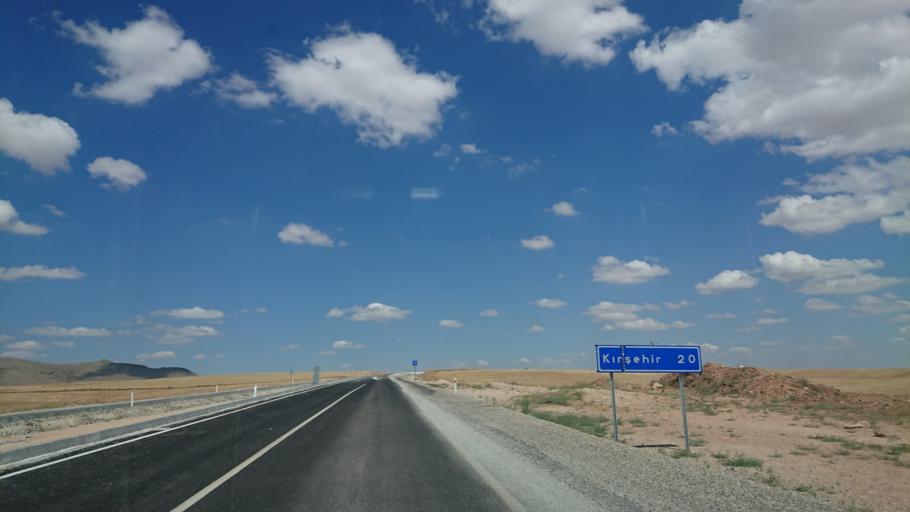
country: TR
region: Aksaray
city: Sariyahsi
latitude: 39.1234
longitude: 33.9718
